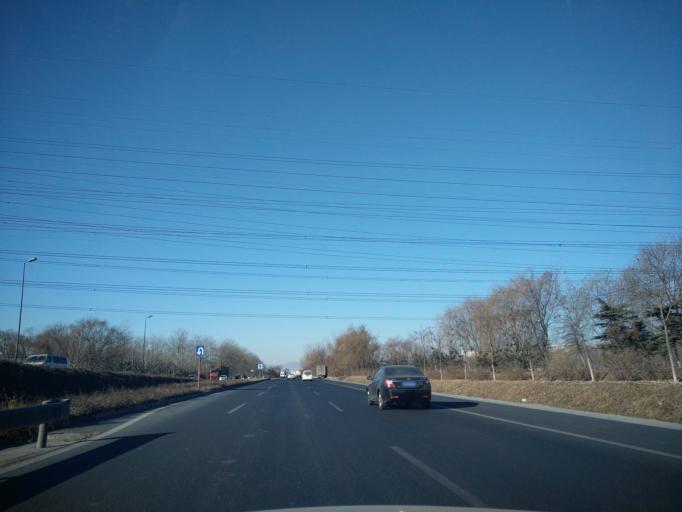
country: CN
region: Beijing
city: Xingfeng
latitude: 39.7201
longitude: 116.3836
